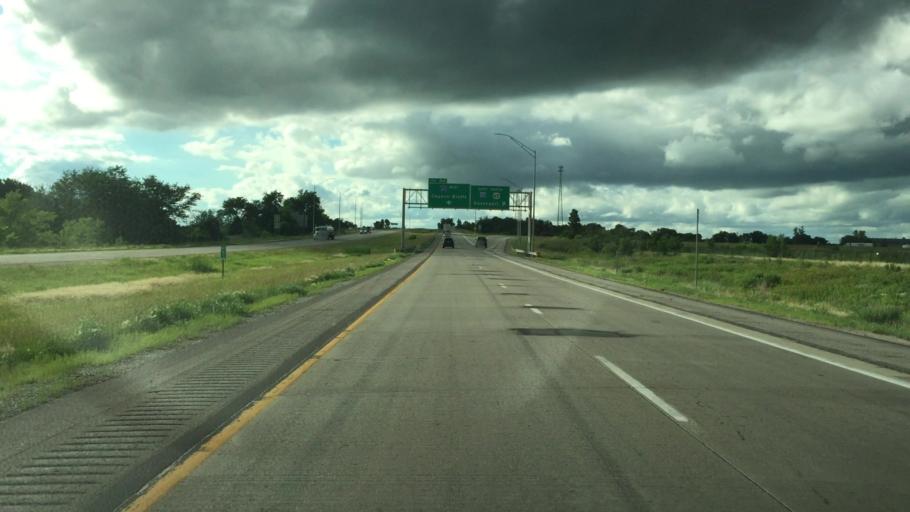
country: US
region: Iowa
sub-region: Polk County
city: Altoona
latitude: 41.6536
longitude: -93.5169
